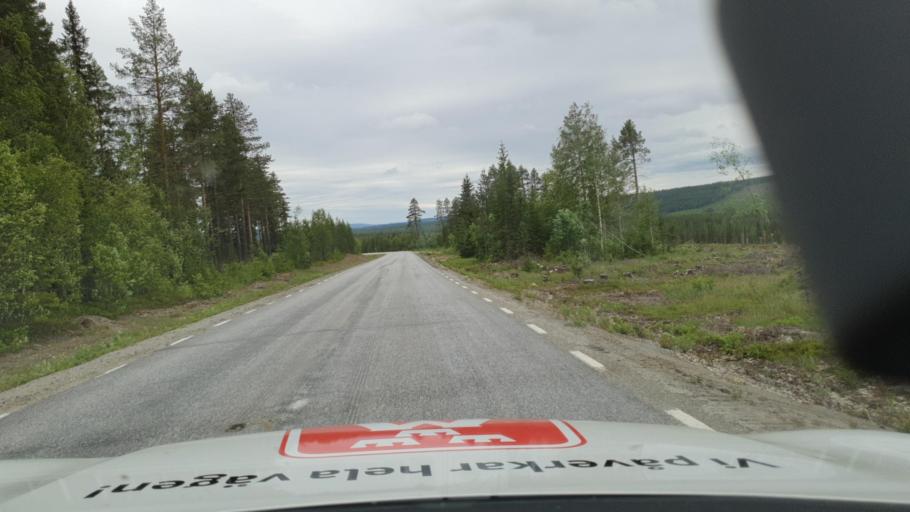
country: SE
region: Vaesterbotten
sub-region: Lycksele Kommun
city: Lycksele
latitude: 64.1310
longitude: 18.3606
